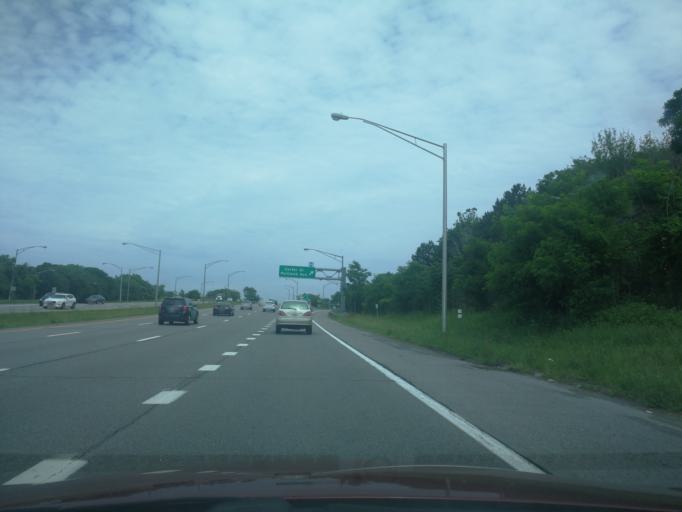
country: US
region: New York
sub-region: Monroe County
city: Irondequoit
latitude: 43.1923
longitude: -77.5959
